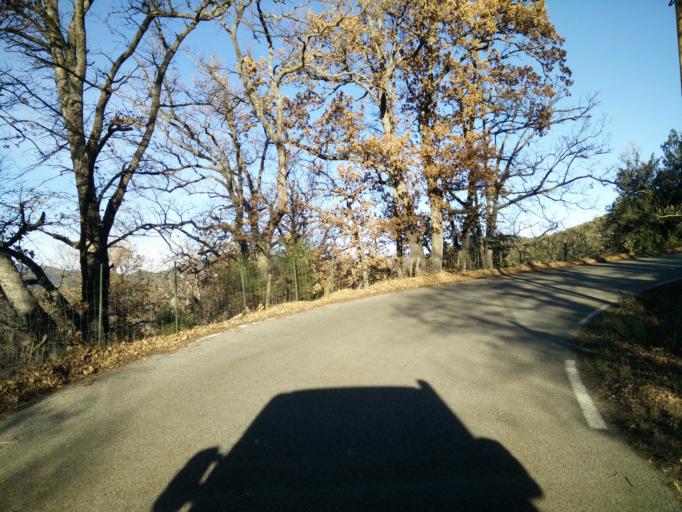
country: FR
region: Provence-Alpes-Cote d'Azur
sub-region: Departement du Var
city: Collobrieres
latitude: 43.2185
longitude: 6.2978
